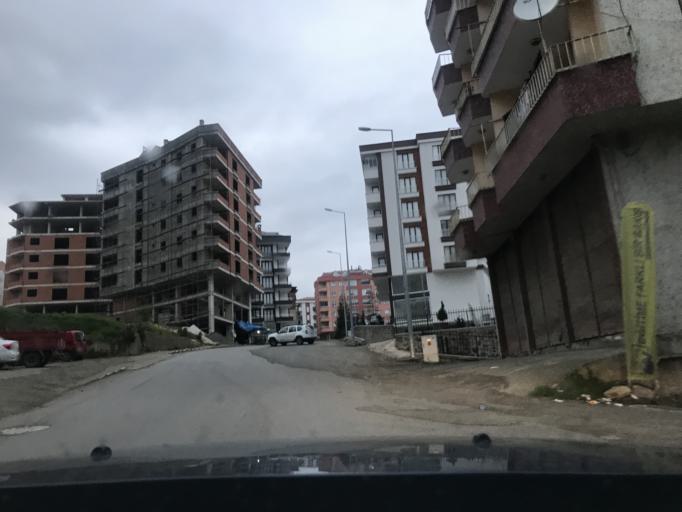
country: TR
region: Trabzon
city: Akcaabat
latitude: 41.0129
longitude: 39.5894
